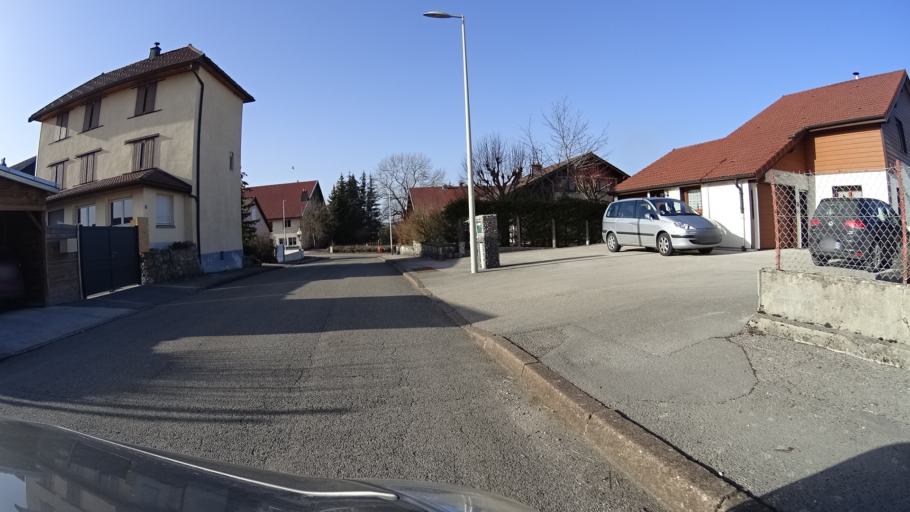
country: FR
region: Franche-Comte
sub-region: Departement du Doubs
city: Frasne
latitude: 46.8918
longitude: 6.2201
